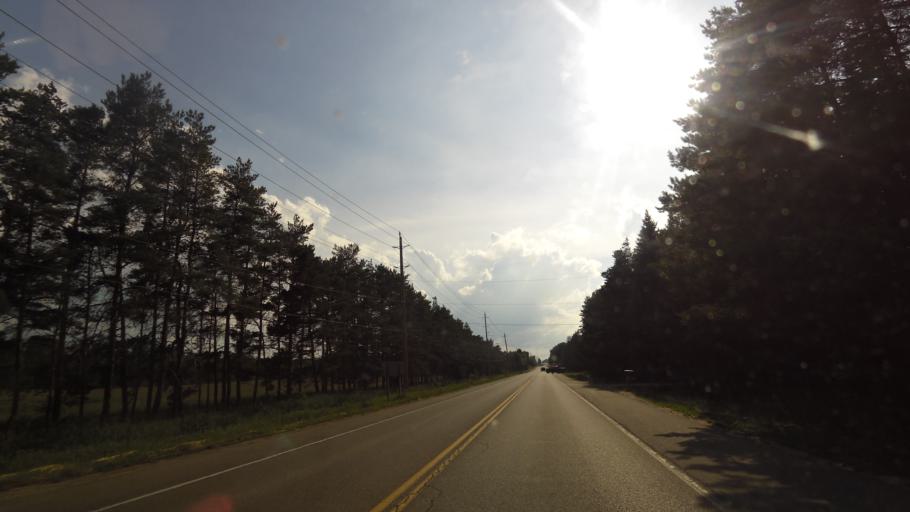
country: CA
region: Ontario
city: Orangeville
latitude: 43.9486
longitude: -80.0929
